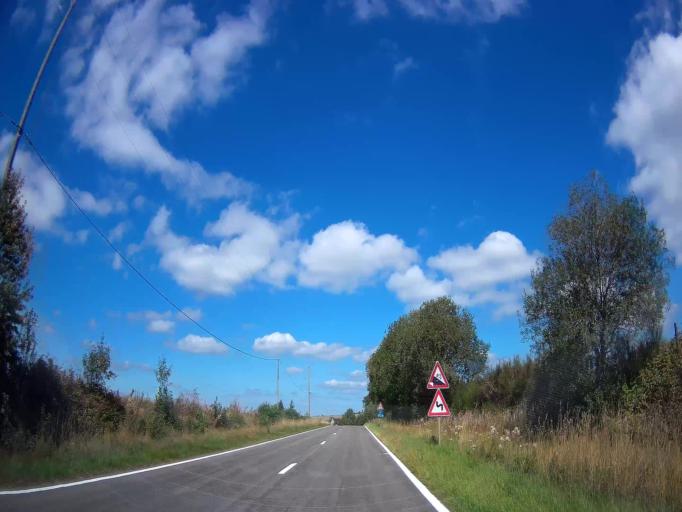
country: BE
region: Wallonia
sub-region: Province du Luxembourg
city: Bertogne
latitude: 50.0434
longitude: 5.6892
